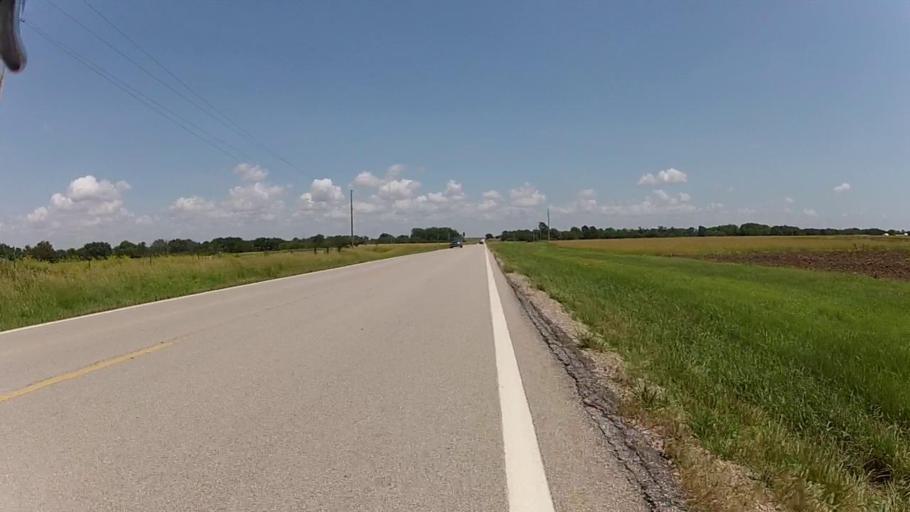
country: US
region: Kansas
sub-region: Montgomery County
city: Cherryvale
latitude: 37.1928
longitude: -95.4557
